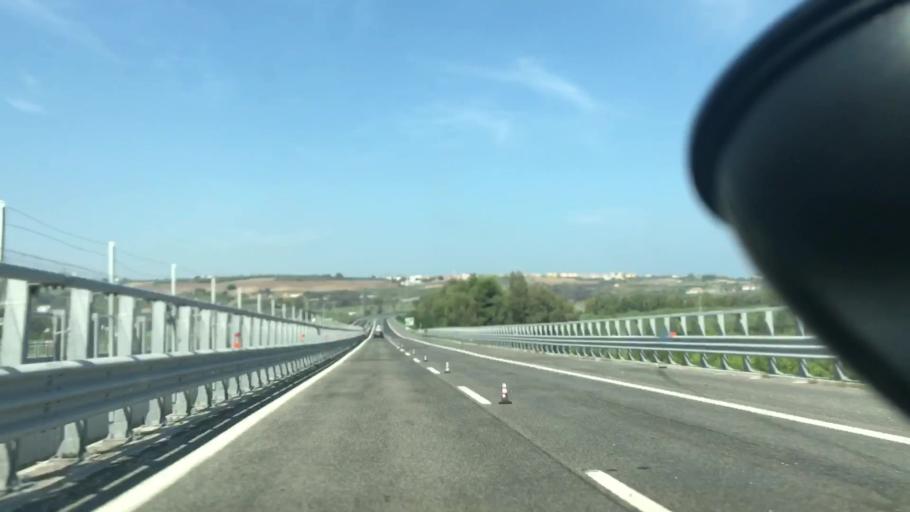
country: IT
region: Molise
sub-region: Provincia di Campobasso
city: Campomarino
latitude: 41.9552
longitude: 15.0143
